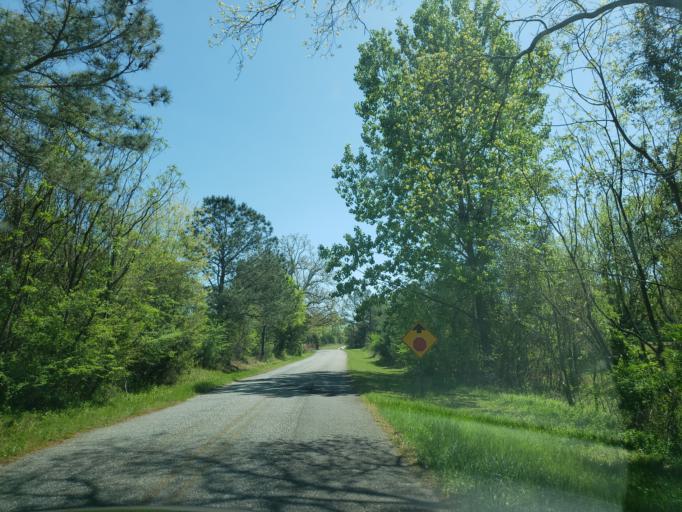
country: US
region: Alabama
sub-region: Tallapoosa County
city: Camp Hill
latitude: 32.6712
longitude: -85.7356
